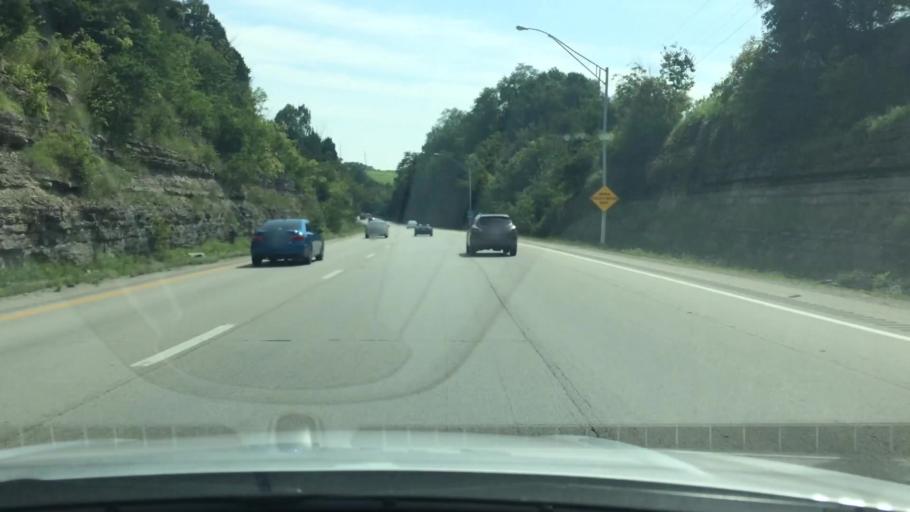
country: US
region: Kentucky
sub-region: Franklin County
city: Frankfort
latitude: 38.1573
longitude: -84.8859
